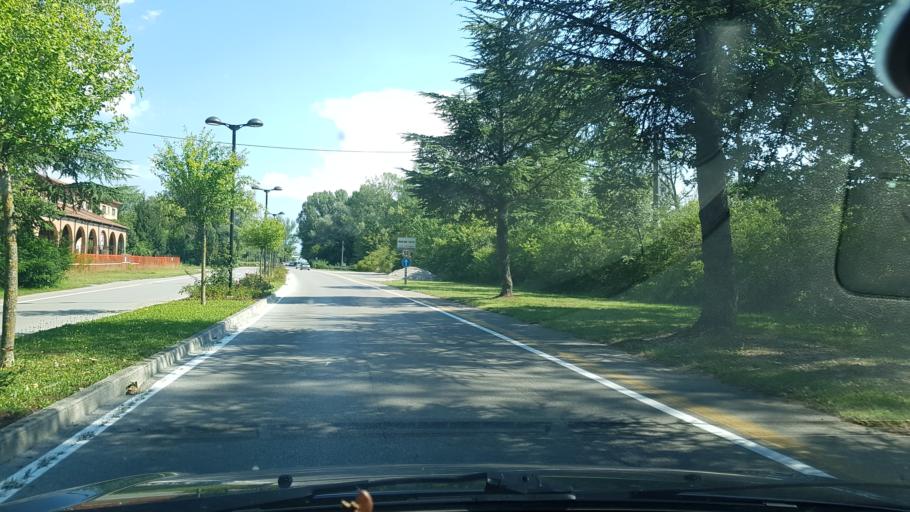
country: IT
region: Friuli Venezia Giulia
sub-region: Provincia di Gorizia
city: Monfalcone
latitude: 45.7804
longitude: 13.5232
